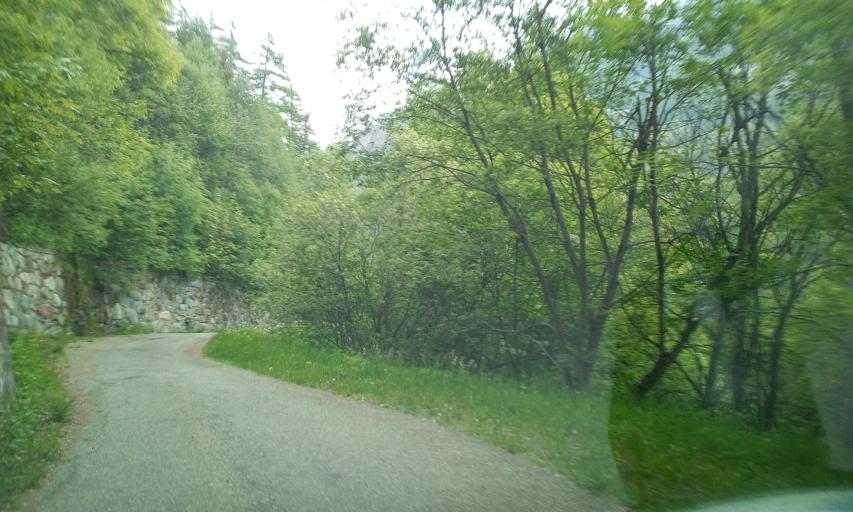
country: IT
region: Aosta Valley
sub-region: Valle d'Aosta
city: Torgnon
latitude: 45.8236
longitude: 7.5742
